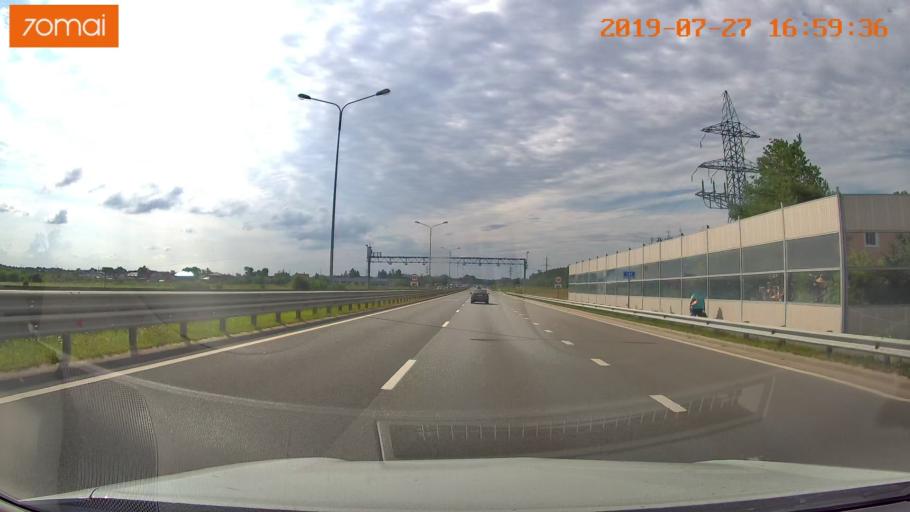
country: RU
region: Kaliningrad
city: Bol'shoe Isakovo
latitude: 54.7047
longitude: 20.6455
